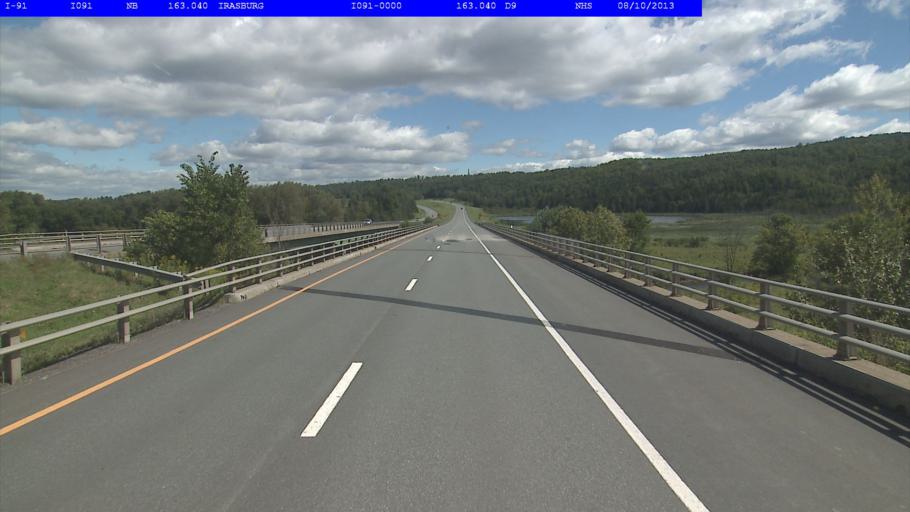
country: US
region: Vermont
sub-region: Orleans County
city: Newport
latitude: 44.8279
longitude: -72.2022
